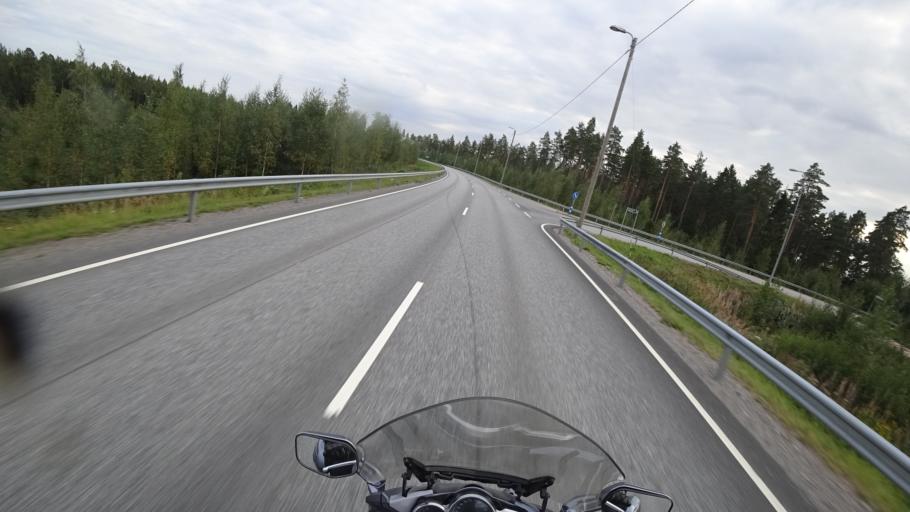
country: FI
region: Uusimaa
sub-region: Raaseporin
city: Karis
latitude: 60.0652
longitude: 23.6300
